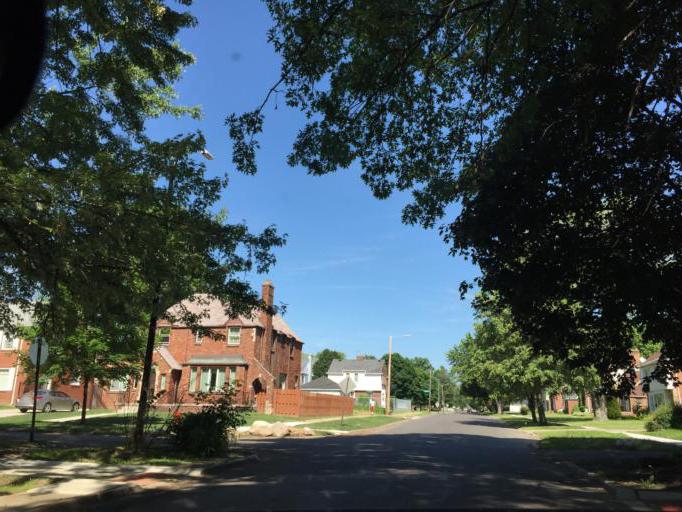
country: US
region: Michigan
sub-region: Oakland County
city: Southfield
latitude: 42.4081
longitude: -83.2278
